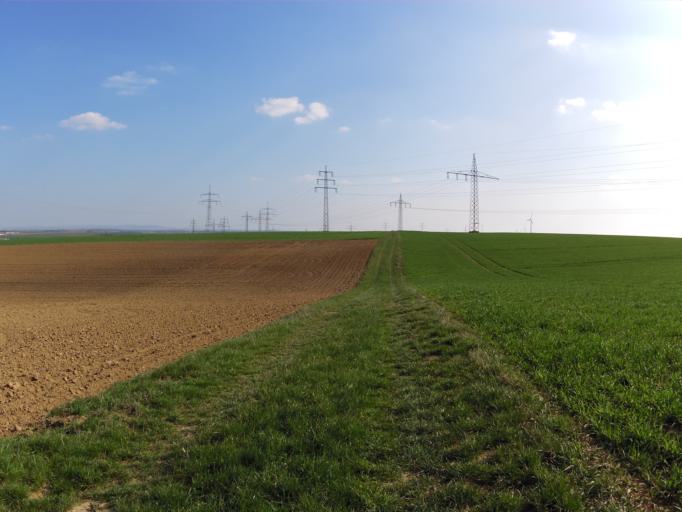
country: DE
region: Bavaria
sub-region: Regierungsbezirk Unterfranken
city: Theilheim
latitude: 49.7697
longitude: 10.0466
